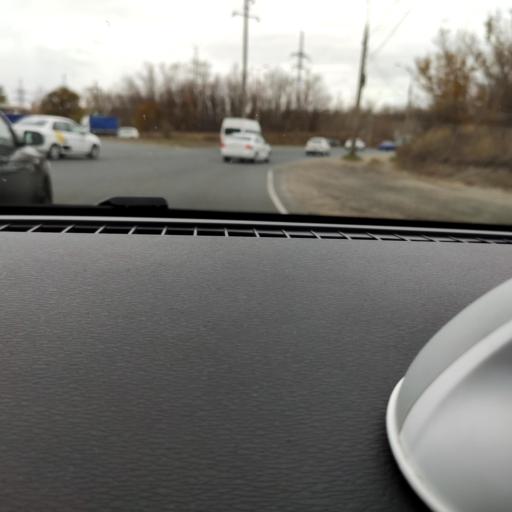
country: RU
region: Samara
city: Samara
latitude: 53.1268
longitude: 50.1715
